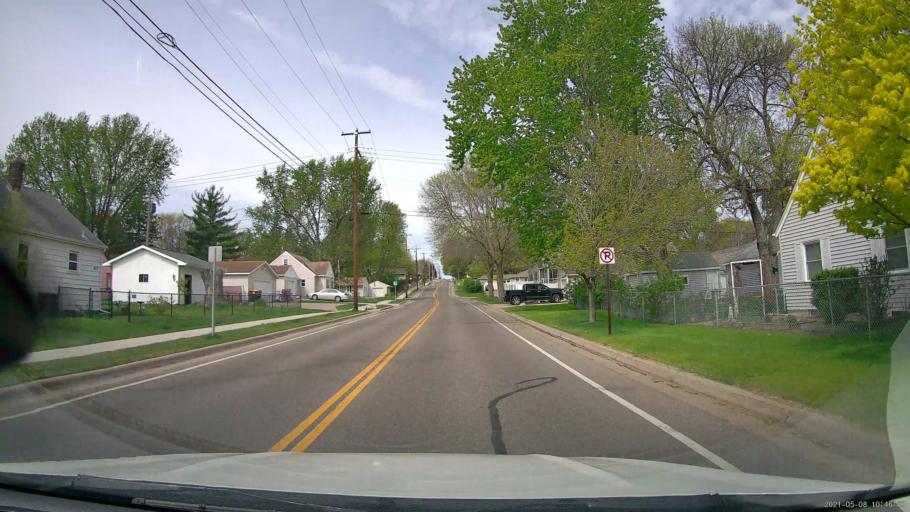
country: US
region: Minnesota
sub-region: Dakota County
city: South Saint Paul
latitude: 44.8980
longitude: -93.0541
